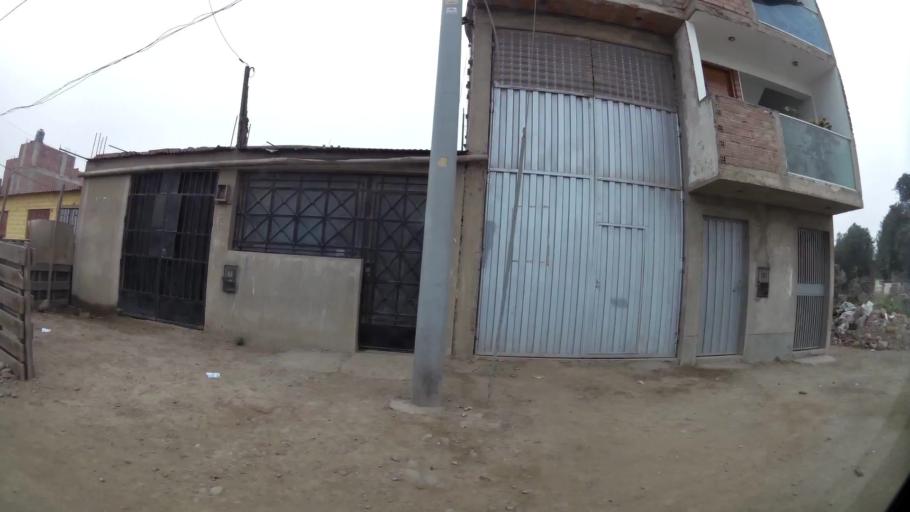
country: PE
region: Lima
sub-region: Lima
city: Carabayllo
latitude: -11.8609
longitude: -77.0221
